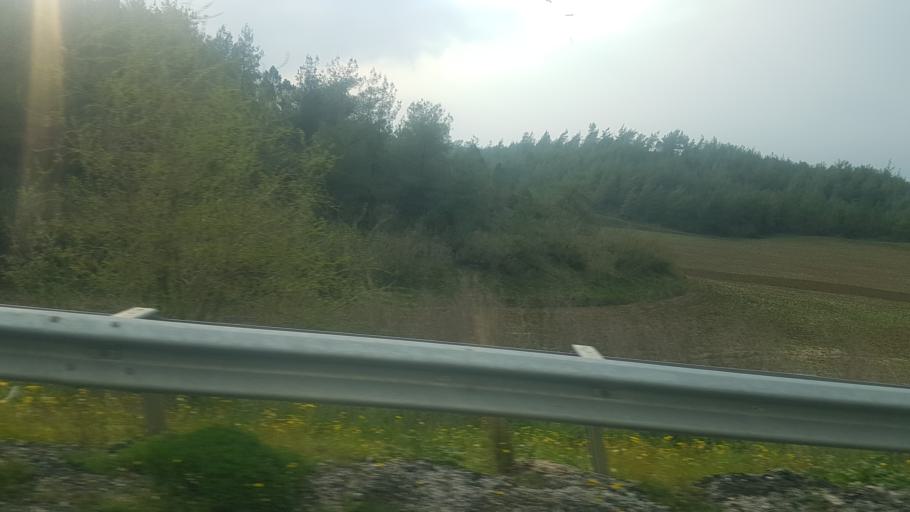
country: TR
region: Mersin
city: Yenice
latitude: 37.0801
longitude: 35.1732
